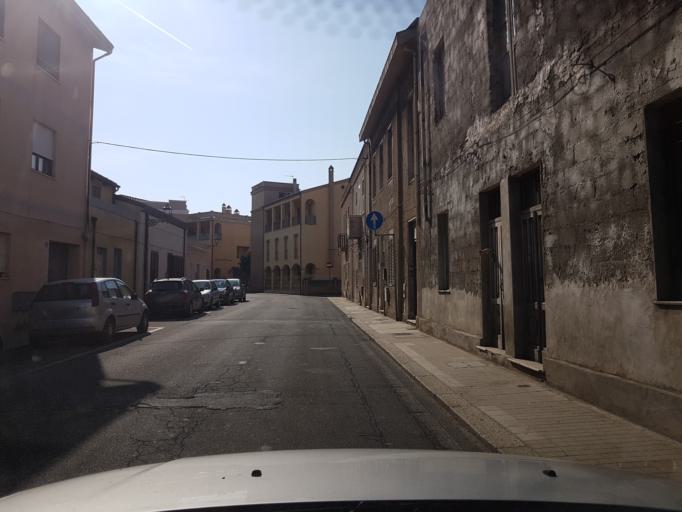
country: IT
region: Sardinia
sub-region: Provincia di Oristano
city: Oristano
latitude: 39.8999
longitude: 8.5932
